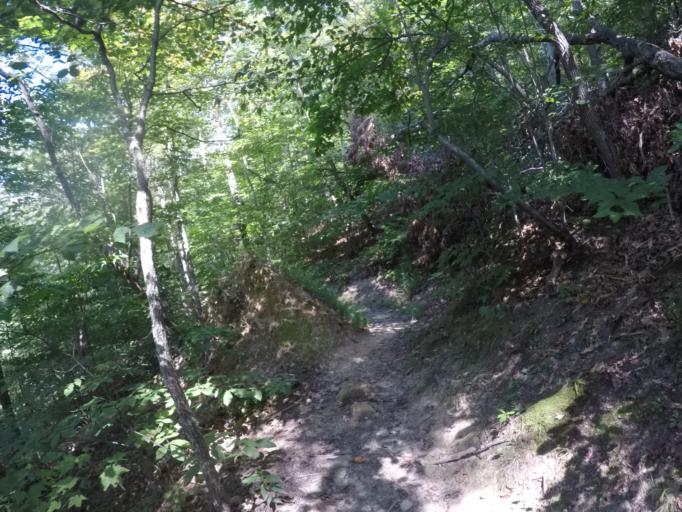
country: US
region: Ohio
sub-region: Lawrence County
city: Ironton
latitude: 38.6266
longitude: -82.6150
